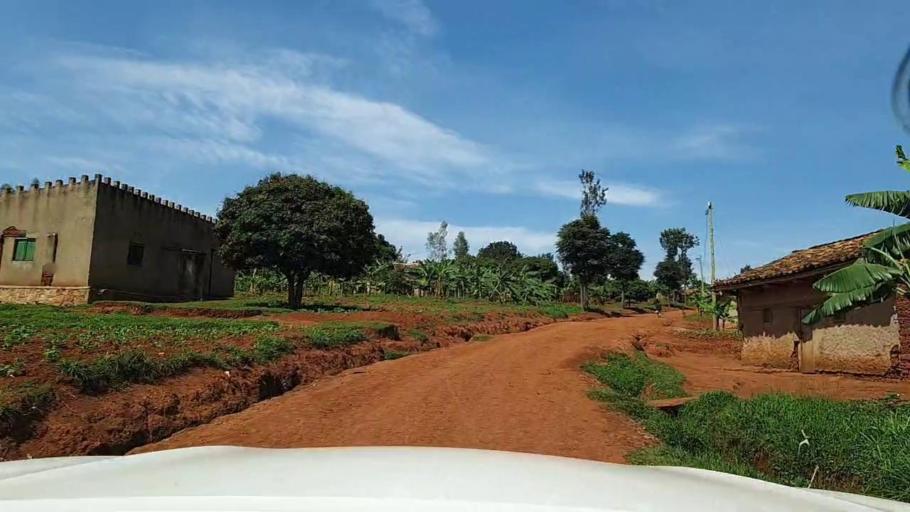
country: RW
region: Southern Province
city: Butare
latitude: -2.6999
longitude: 29.8533
